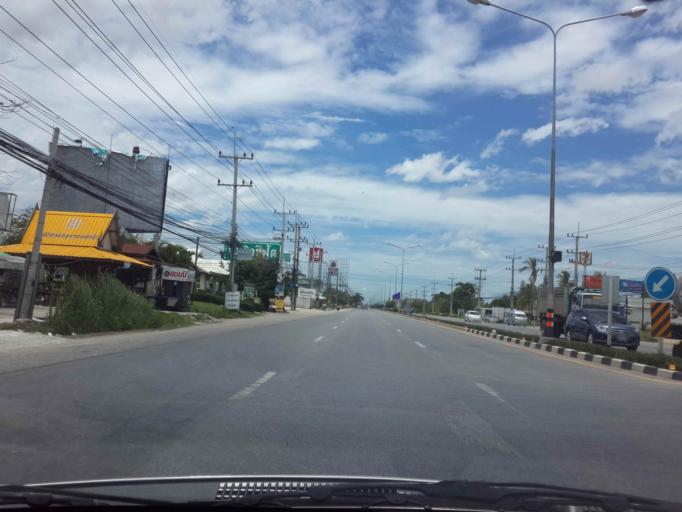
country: TH
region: Prachuap Khiri Khan
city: Hua Hin
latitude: 12.6681
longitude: 99.9524
